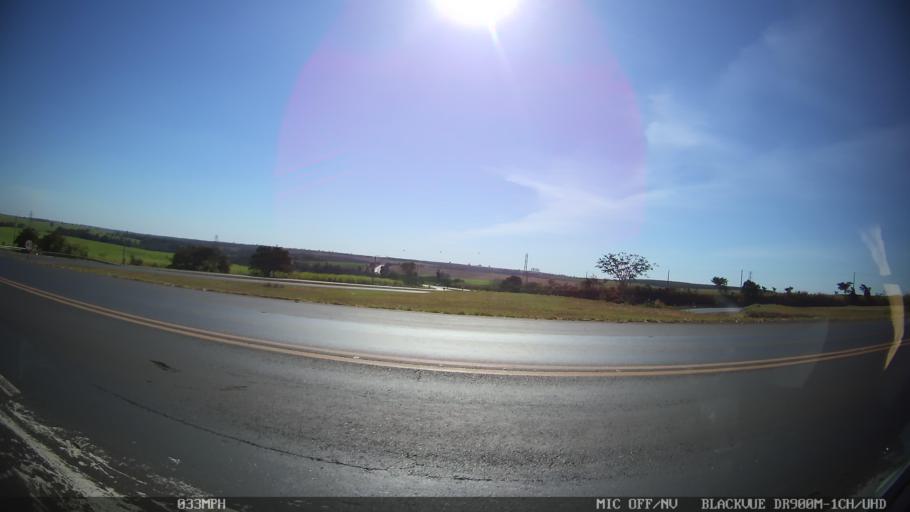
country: BR
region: Sao Paulo
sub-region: Olimpia
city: Olimpia
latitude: -20.6847
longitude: -48.9042
